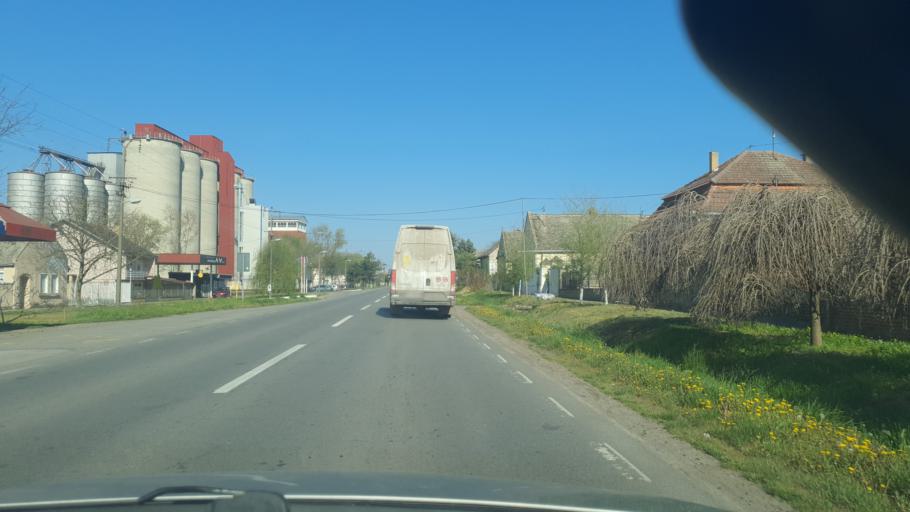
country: RS
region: Autonomna Pokrajina Vojvodina
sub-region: Zapadnobacki Okrug
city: Kula
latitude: 45.6910
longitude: 19.3845
